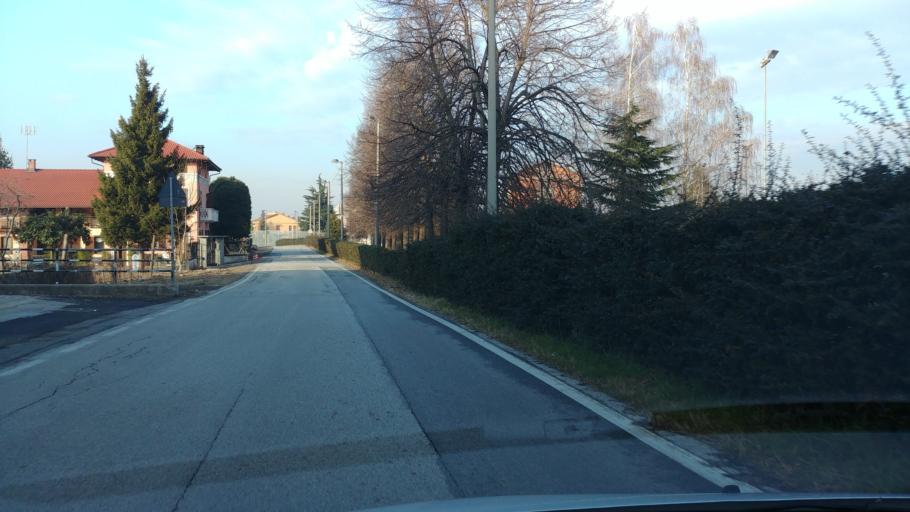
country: IT
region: Piedmont
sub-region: Provincia di Cuneo
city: Cuneo
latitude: 44.4008
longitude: 7.5368
